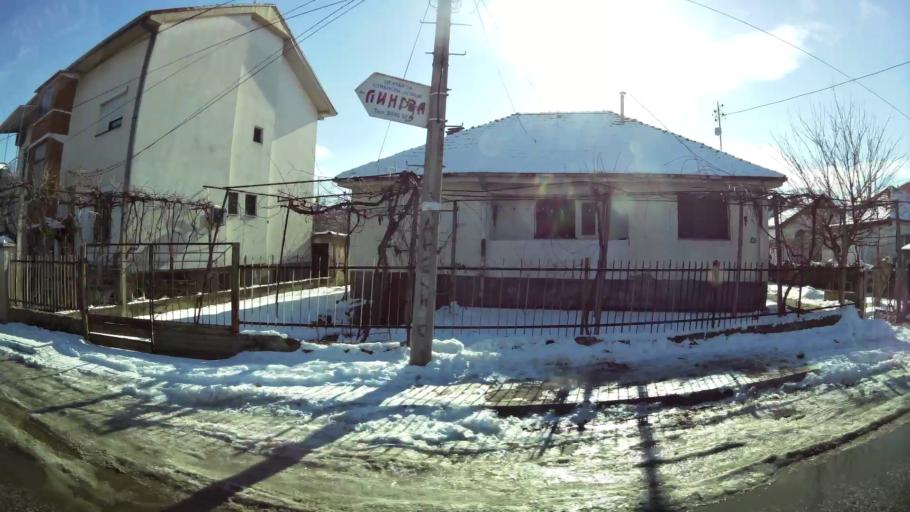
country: MK
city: Krushopek
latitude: 42.0037
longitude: 21.3554
